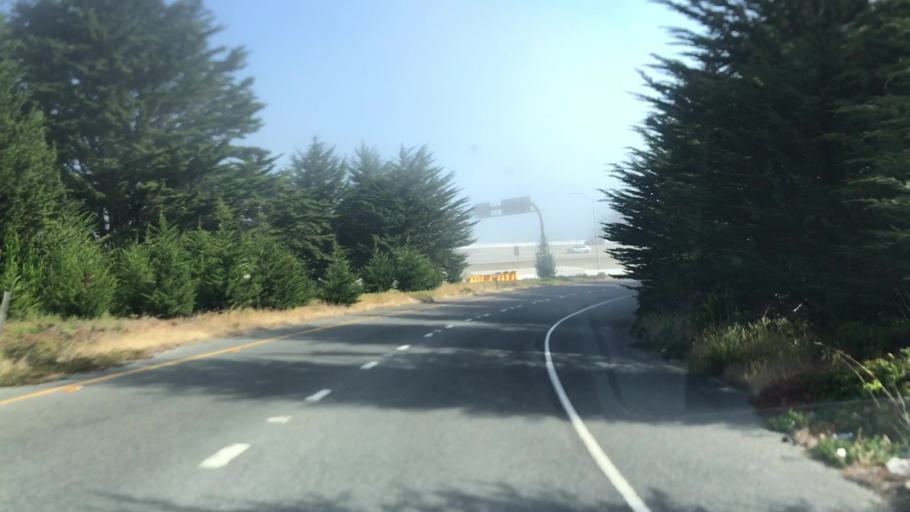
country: US
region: California
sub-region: San Mateo County
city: Broadmoor
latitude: 37.6687
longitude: -122.4836
